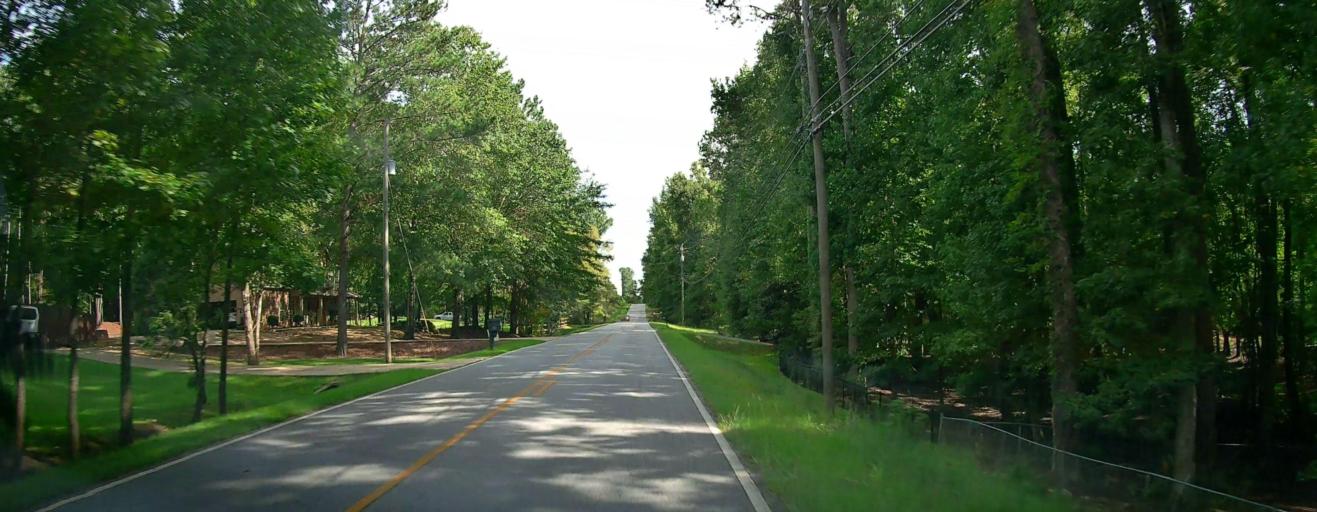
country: US
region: Alabama
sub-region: Lee County
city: Smiths Station
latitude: 32.6034
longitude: -84.9814
